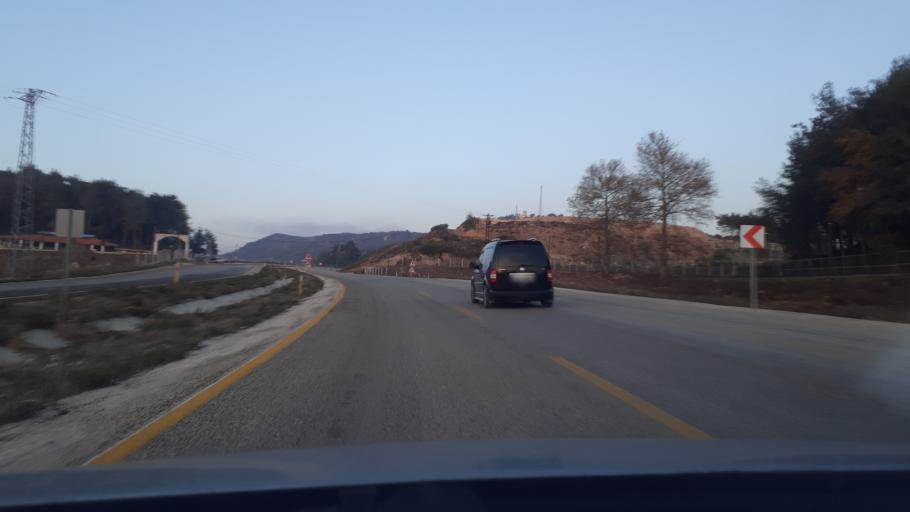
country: TR
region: Hatay
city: Yayladagi
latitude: 35.8920
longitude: 36.0930
